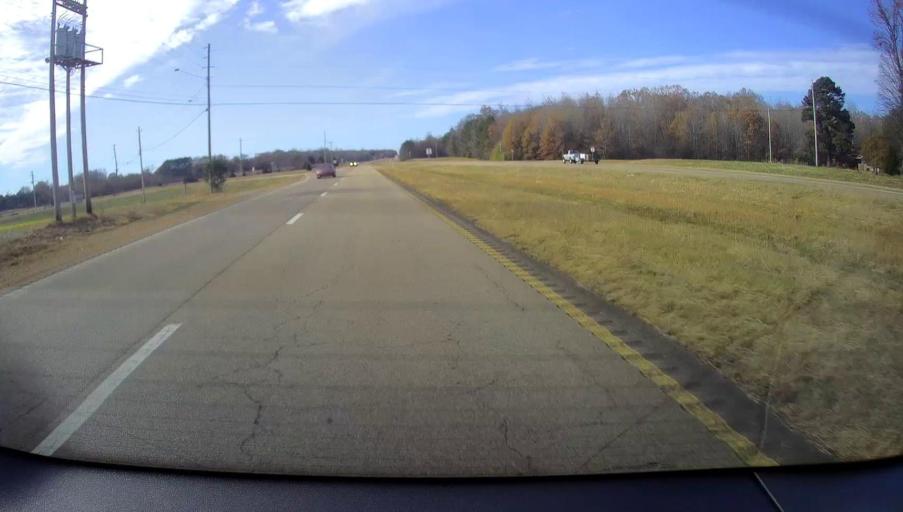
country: US
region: Mississippi
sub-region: Alcorn County
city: Corinth
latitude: 34.9311
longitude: -88.6277
